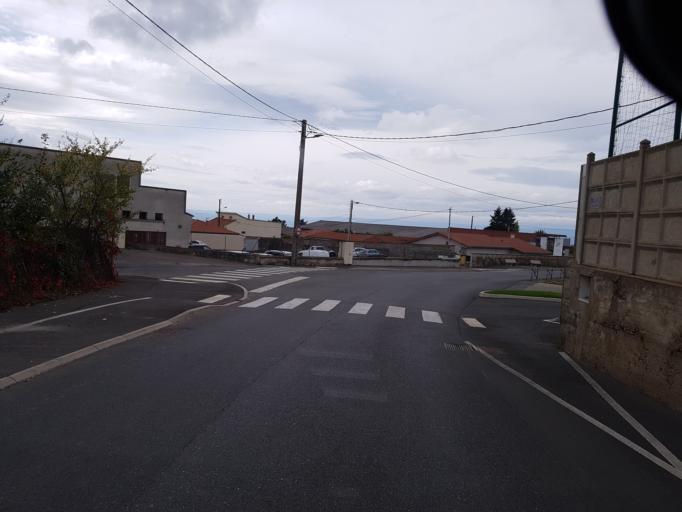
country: FR
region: Rhone-Alpes
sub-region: Departement de la Loire
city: Chazelles-sur-Lyon
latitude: 45.6347
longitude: 4.3842
